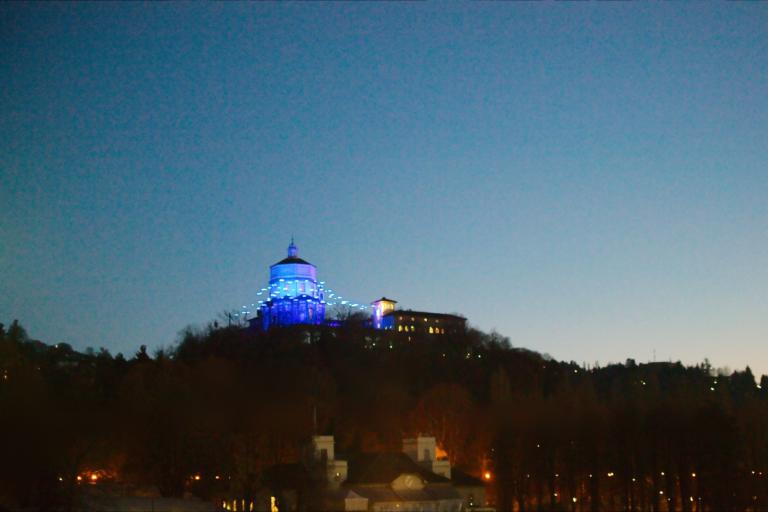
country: IT
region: Piedmont
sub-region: Provincia di Torino
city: Turin
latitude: 45.0635
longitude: 7.6953
